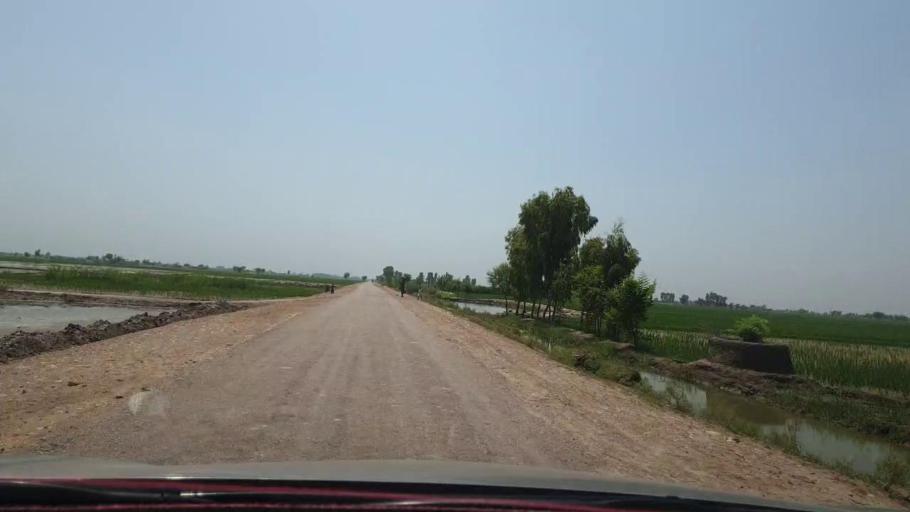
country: PK
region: Sindh
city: Warah
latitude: 27.5644
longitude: 67.8017
